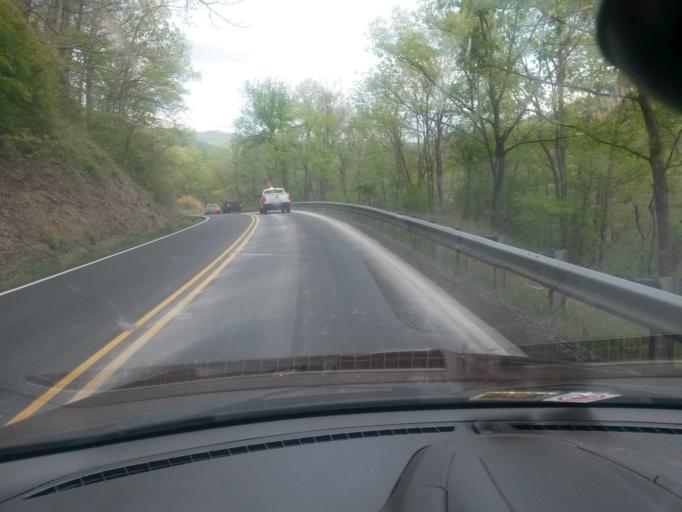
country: US
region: Virginia
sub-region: City of Covington
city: Covington
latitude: 37.7964
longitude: -80.0074
